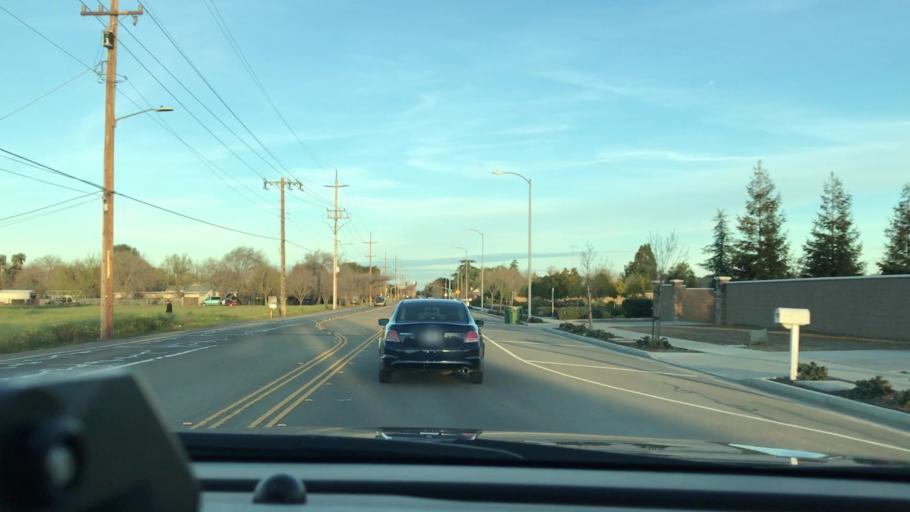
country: US
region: California
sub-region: Contra Costa County
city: Brentwood
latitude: 37.9616
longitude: -121.7085
